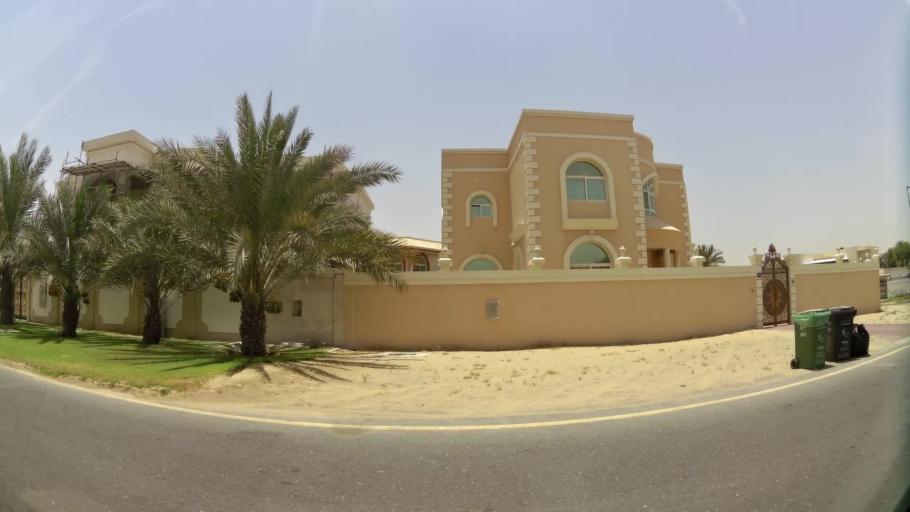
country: AE
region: Ash Shariqah
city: Sharjah
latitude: 25.2532
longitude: 55.4589
